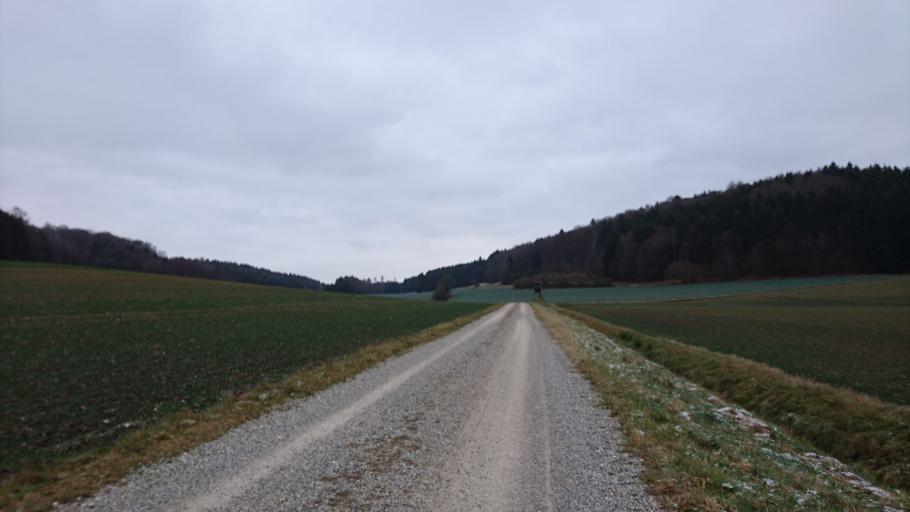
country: DE
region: Bavaria
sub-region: Swabia
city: Zusmarshausen
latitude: 48.4285
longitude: 10.6029
